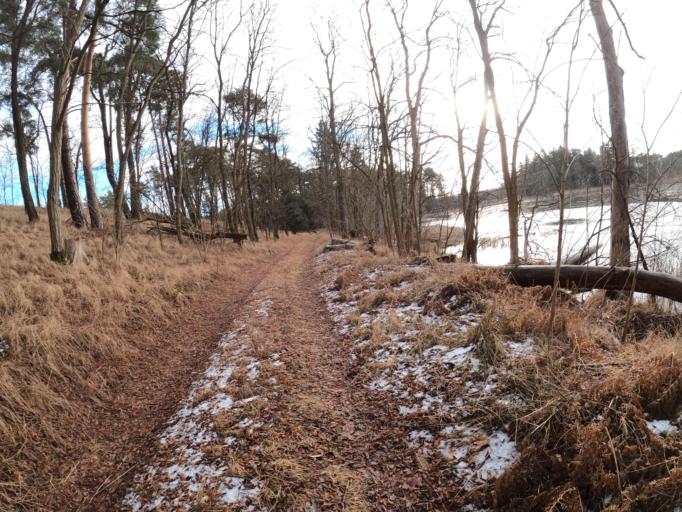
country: PL
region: Lubusz
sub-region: Powiat slubicki
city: Cybinka
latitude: 52.2618
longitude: 14.7929
